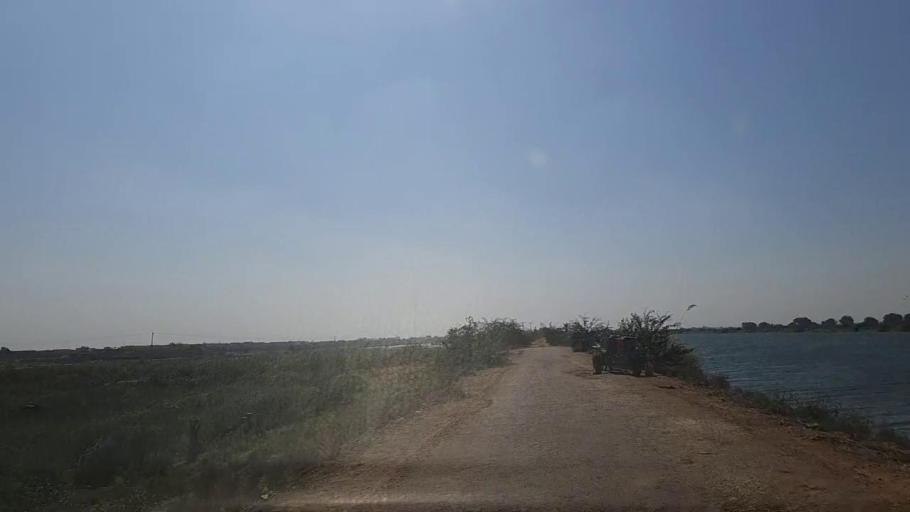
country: PK
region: Sindh
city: Thatta
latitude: 24.8248
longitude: 67.9918
